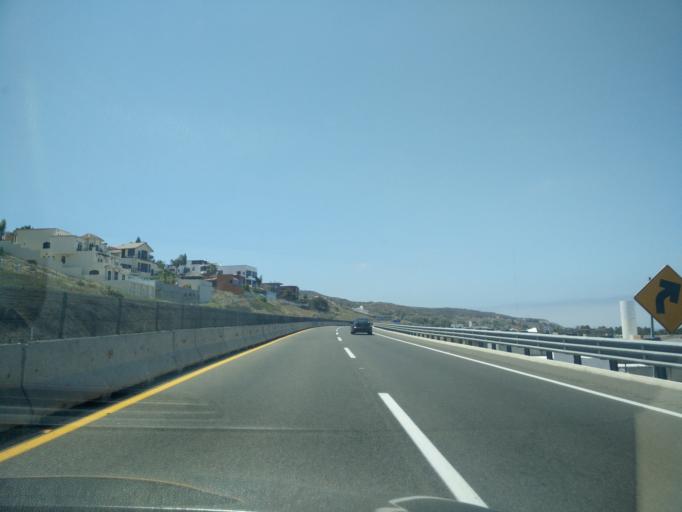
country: MX
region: Baja California
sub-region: Tijuana
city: La Esperanza [Granjas Familiares]
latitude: 32.5205
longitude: -117.1078
